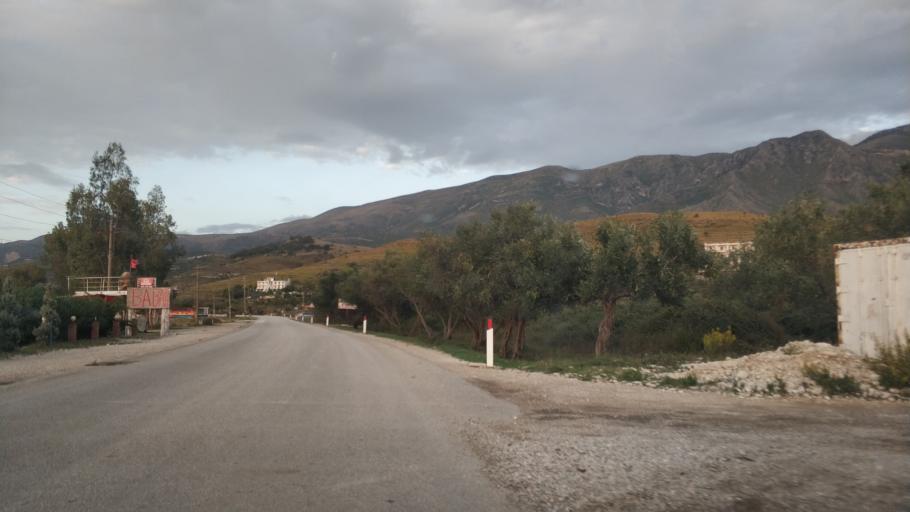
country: AL
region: Vlore
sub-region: Rrethi i Vlores
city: Orikum
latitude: 40.3454
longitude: 19.4843
